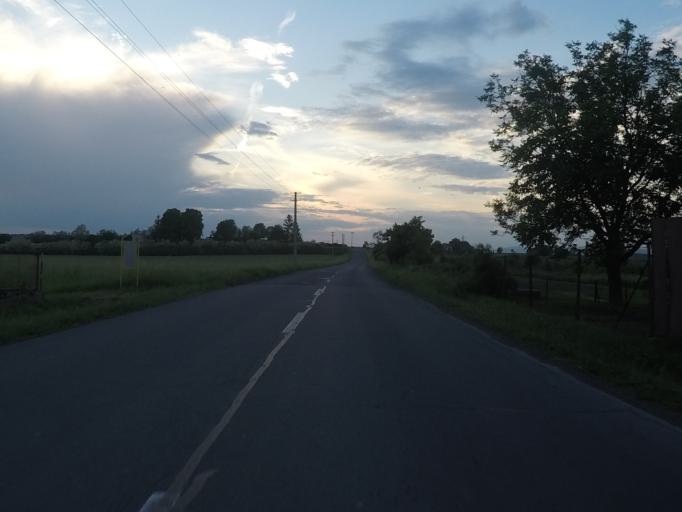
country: SK
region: Banskobystricky
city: Fil'akovo
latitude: 48.3499
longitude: 19.8363
